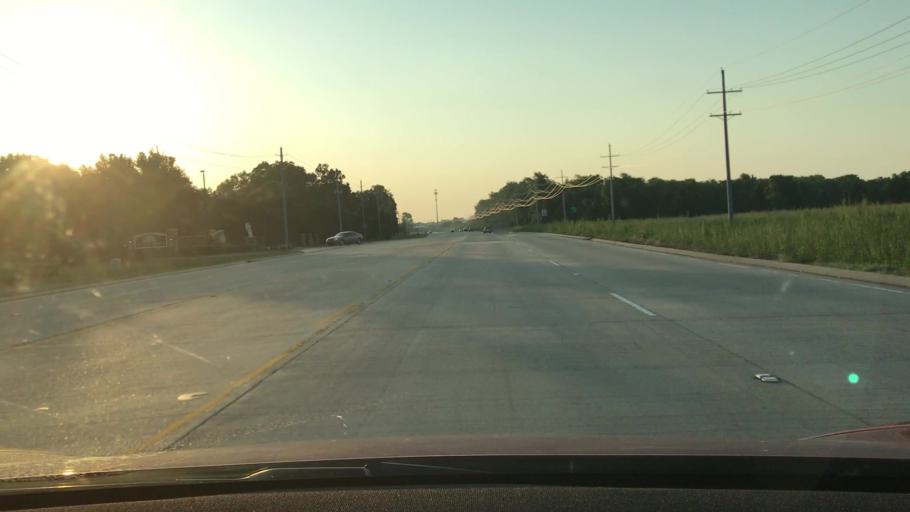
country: US
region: Louisiana
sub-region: Bossier Parish
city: Bossier City
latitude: 32.4009
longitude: -93.7043
